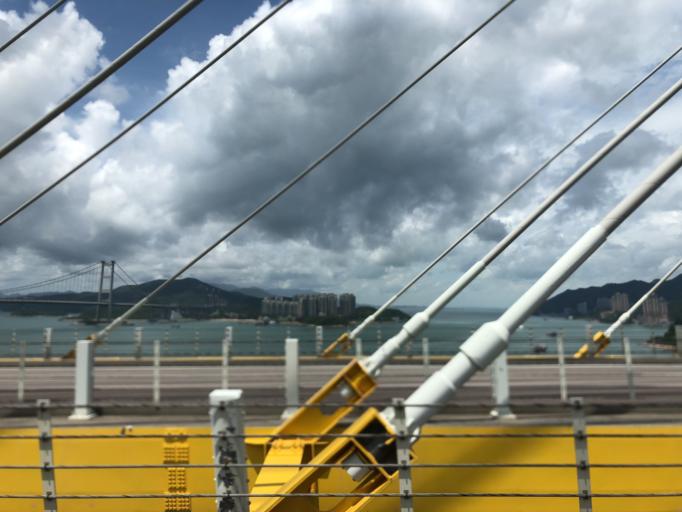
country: HK
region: Tsuen Wan
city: Tsuen Wan
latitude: 22.3633
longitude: 114.0802
